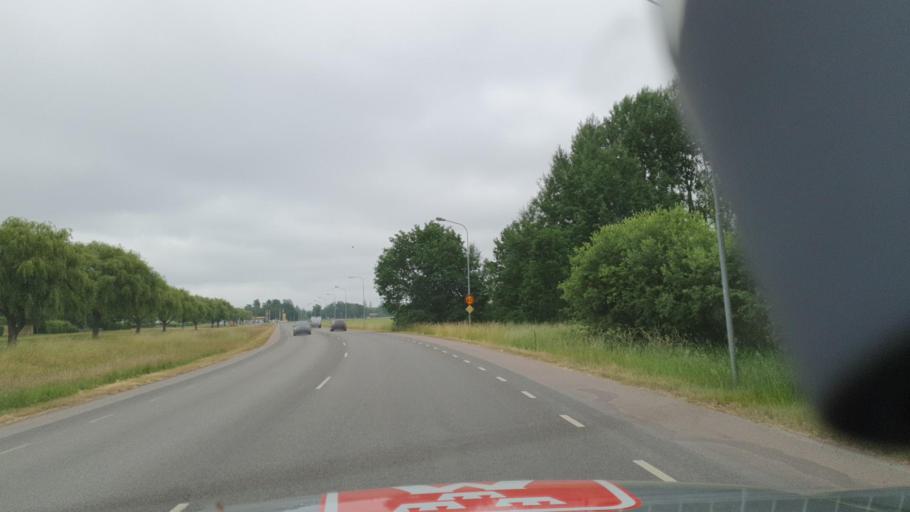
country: SE
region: Kalmar
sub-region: Kalmar Kommun
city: Lindsdal
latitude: 56.7242
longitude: 16.2922
